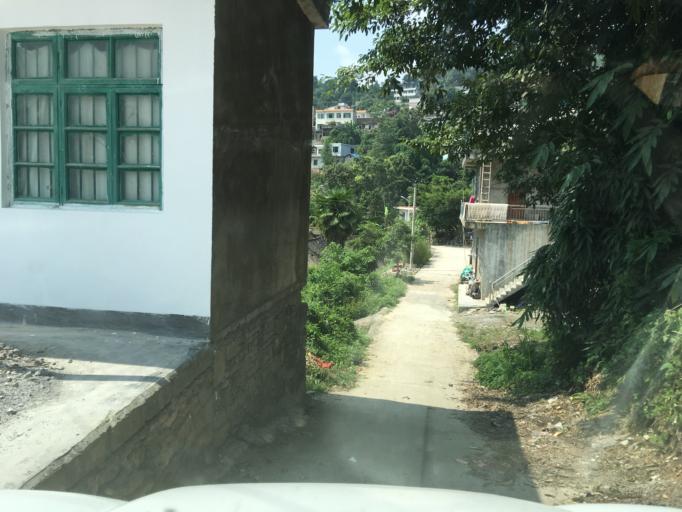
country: CN
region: Guangxi Zhuangzu Zizhiqu
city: Xinzhou
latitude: 24.9940
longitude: 105.7575
